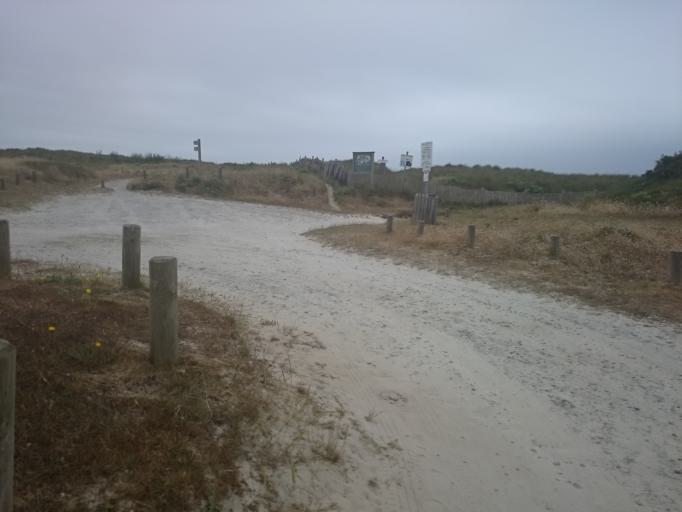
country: FR
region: Brittany
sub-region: Departement du Finistere
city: Saint-Pabu
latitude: 48.5765
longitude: -4.6320
